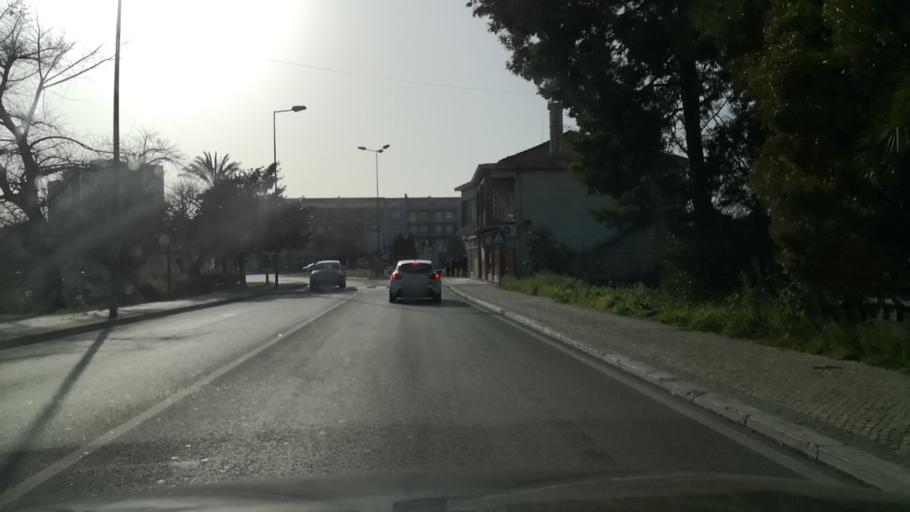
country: PT
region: Leiria
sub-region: Marinha Grande
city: Marinha Grande
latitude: 39.7470
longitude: -8.9327
